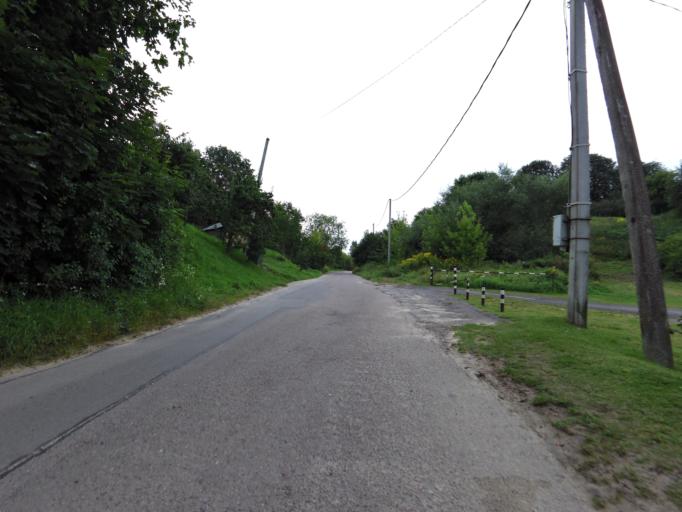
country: LT
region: Vilnius County
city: Rasos
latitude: 54.6617
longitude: 25.2916
